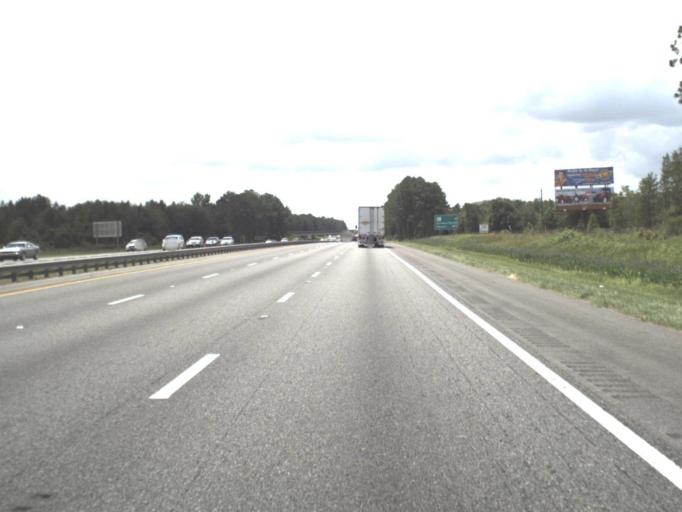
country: US
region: Florida
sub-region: Columbia County
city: Lake City
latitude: 30.1698
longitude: -82.6836
